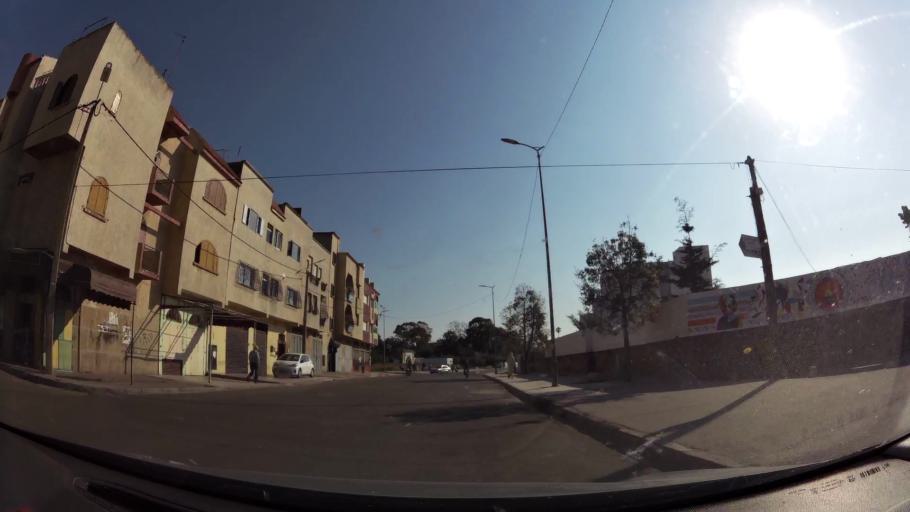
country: MA
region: Rabat-Sale-Zemmour-Zaer
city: Sale
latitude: 34.0449
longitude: -6.8156
